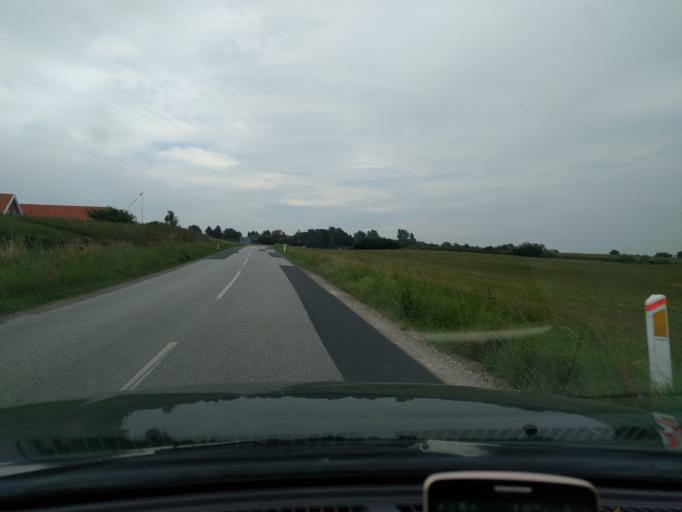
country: DK
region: Zealand
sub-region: Slagelse Kommune
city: Skaelskor
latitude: 55.3043
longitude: 11.2572
